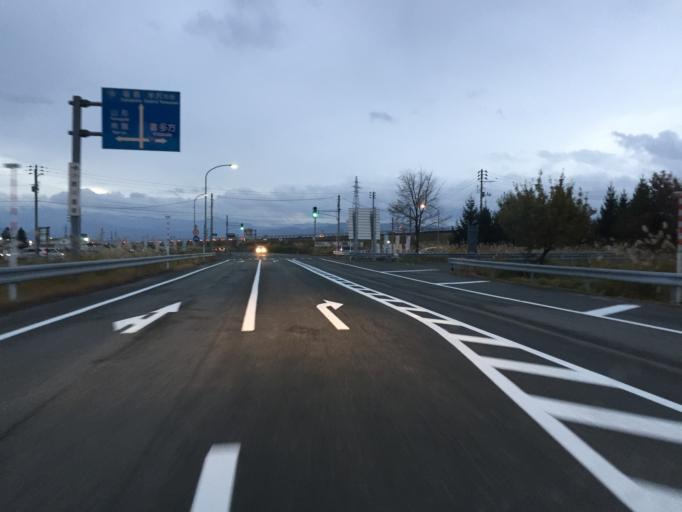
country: JP
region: Yamagata
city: Yonezawa
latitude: 37.9515
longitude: 140.1166
